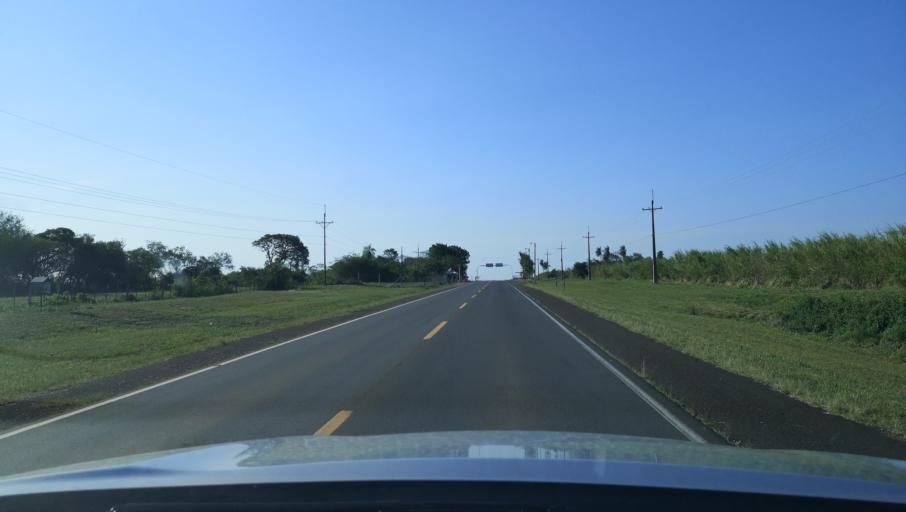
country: PY
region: Misiones
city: Santa Maria
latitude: -26.7847
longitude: -57.0265
